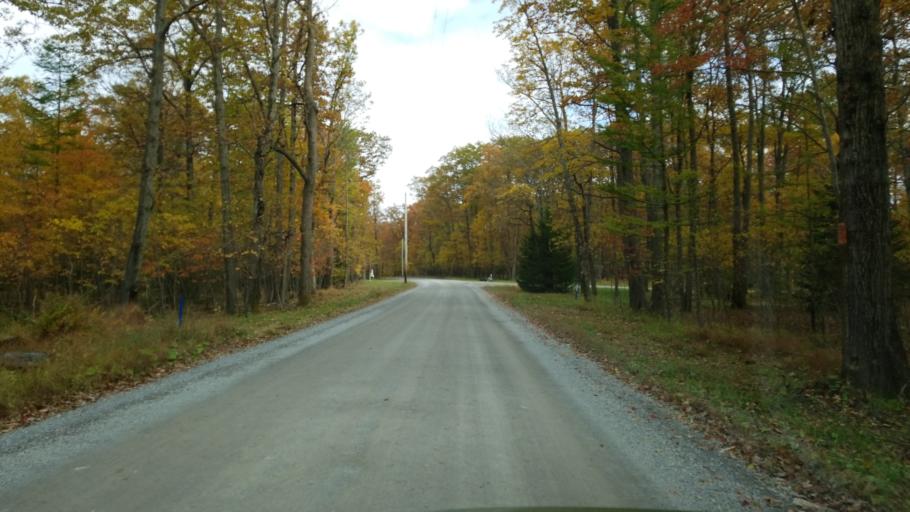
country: US
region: Pennsylvania
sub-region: Clearfield County
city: Clearfield
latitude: 41.1608
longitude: -78.4527
